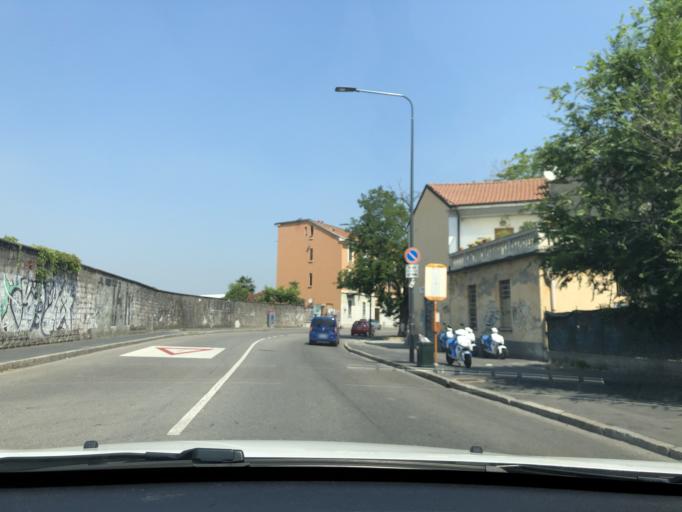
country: IT
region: Lombardy
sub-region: Citta metropolitana di Milano
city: Novate Milanese
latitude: 45.5074
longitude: 9.1597
